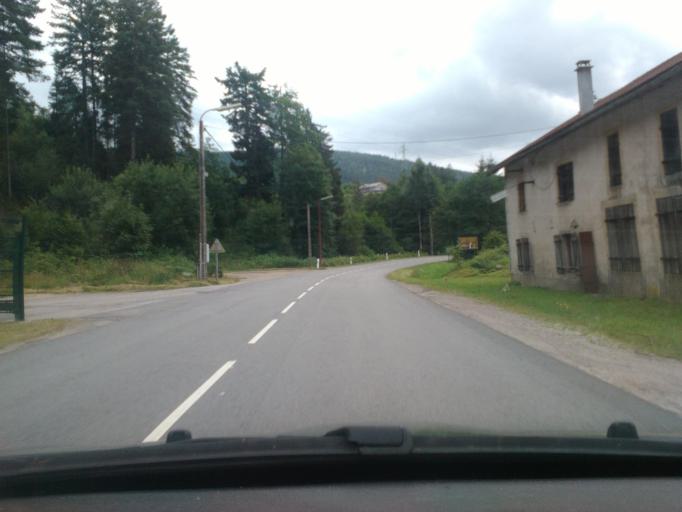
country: FR
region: Lorraine
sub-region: Departement des Vosges
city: Gerardmer
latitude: 48.0877
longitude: 6.8924
